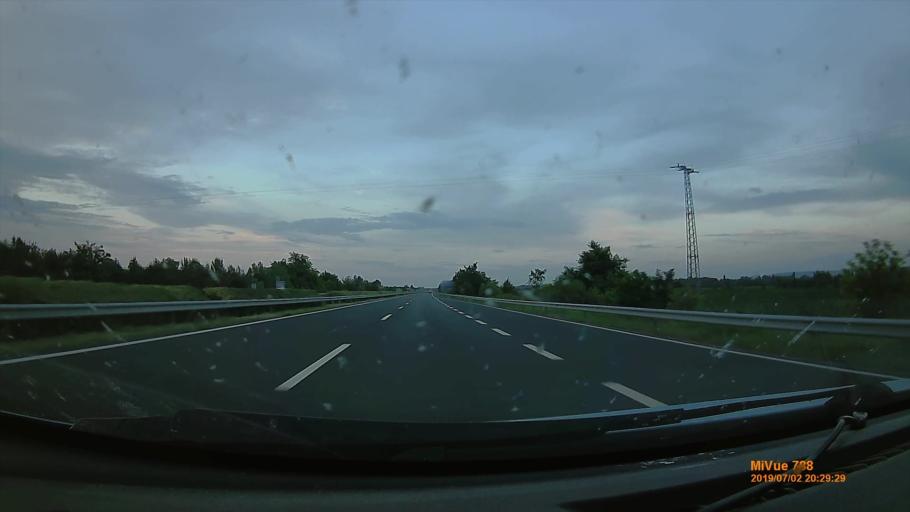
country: HU
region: Somogy
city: Fonyod
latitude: 46.7244
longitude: 17.5856
